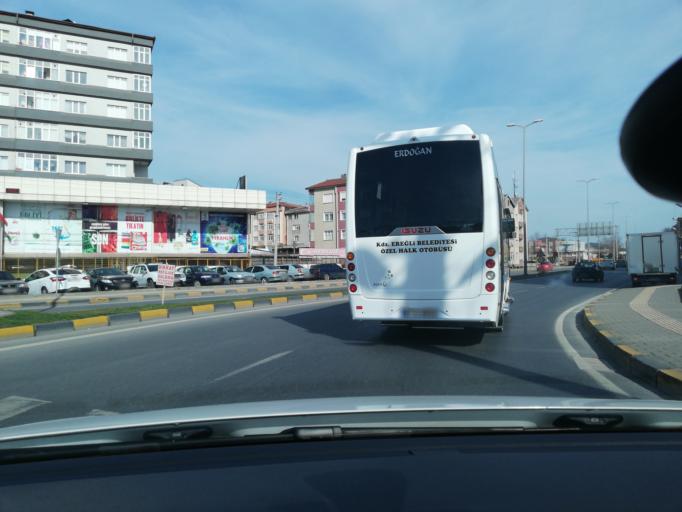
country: TR
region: Zonguldak
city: Eregli
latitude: 41.2695
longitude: 31.4356
